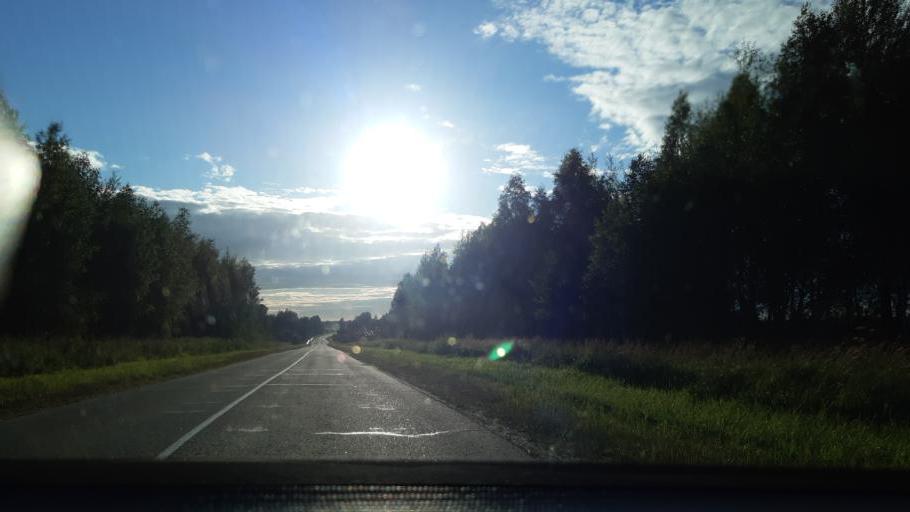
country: RU
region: Smolensk
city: Yel'nya
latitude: 54.5589
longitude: 33.1757
